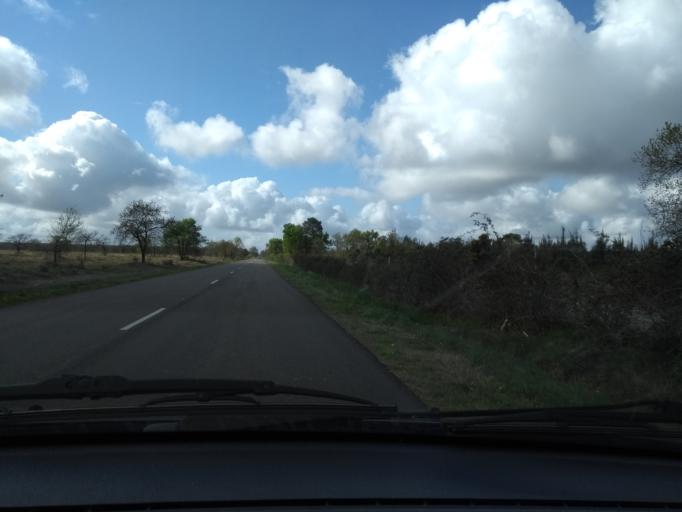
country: FR
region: Aquitaine
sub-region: Departement des Landes
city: Pontenx-les-Forges
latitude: 44.2677
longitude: -1.1020
